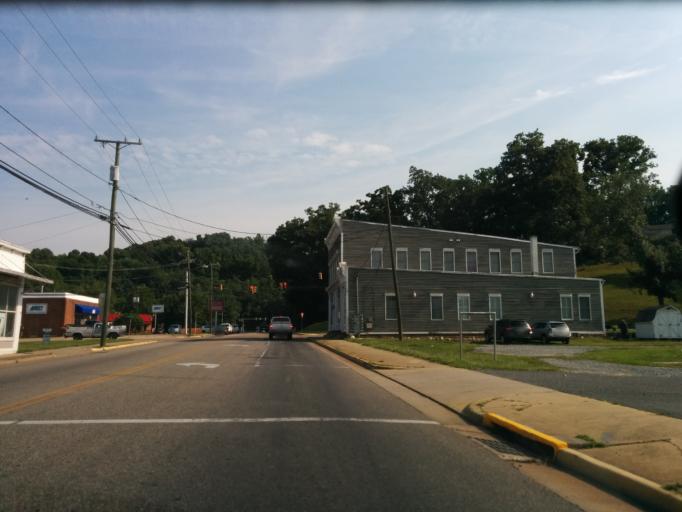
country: US
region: Virginia
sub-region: City of Buena Vista
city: Buena Vista
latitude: 37.7406
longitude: -79.3549
